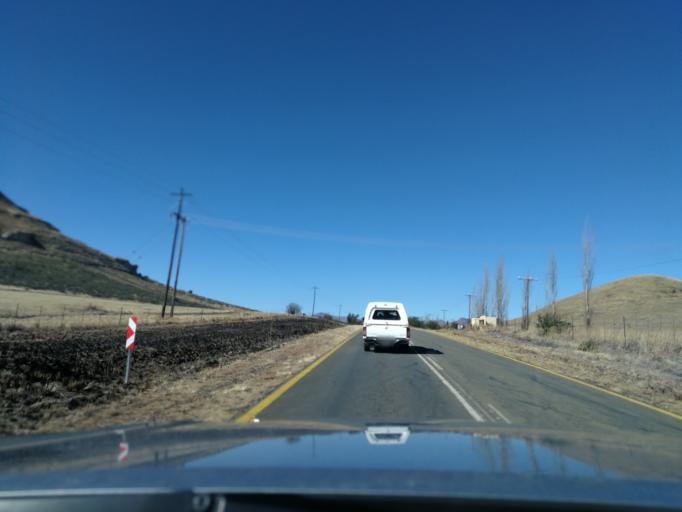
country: LS
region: Butha-Buthe
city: Butha-Buthe
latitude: -28.5183
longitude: 28.4417
